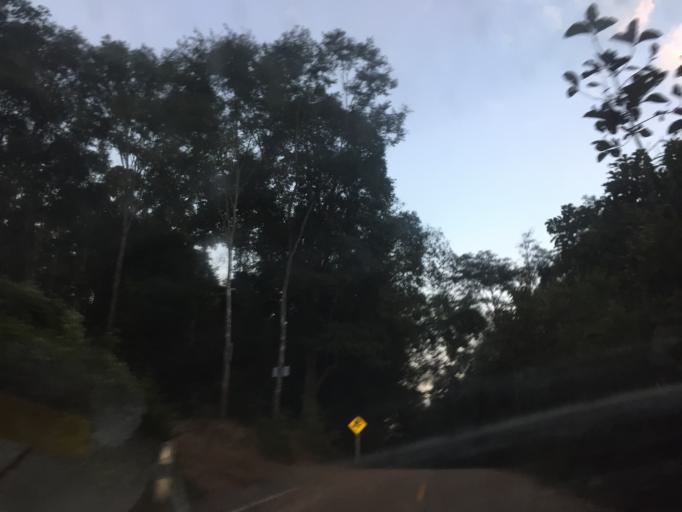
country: TH
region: Chiang Mai
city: Samoeng
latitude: 18.9965
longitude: 98.7174
